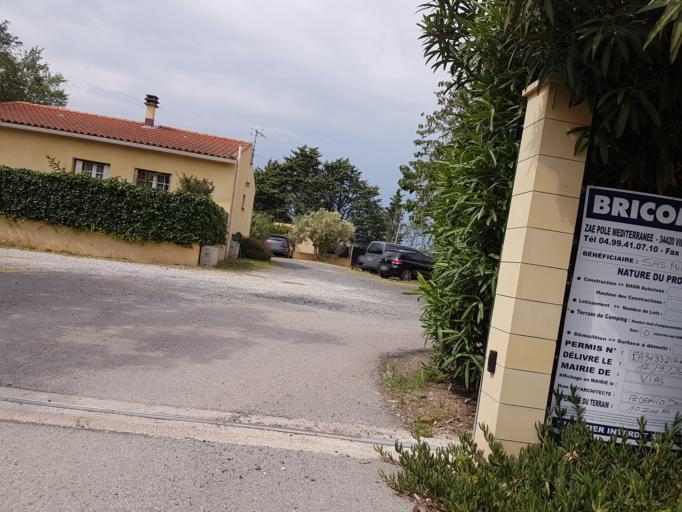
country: FR
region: Languedoc-Roussillon
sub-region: Departement de l'Herault
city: Vias
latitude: 43.3140
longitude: 3.3829
